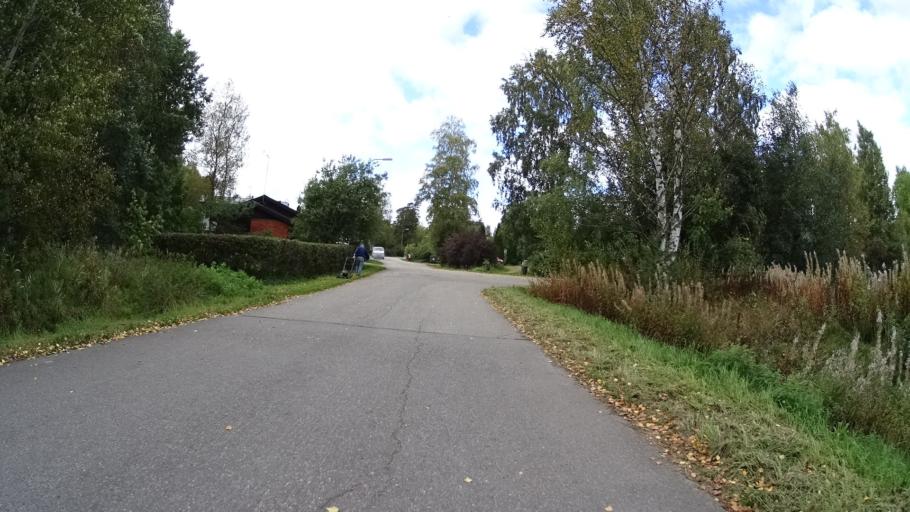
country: FI
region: Uusimaa
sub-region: Helsinki
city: Helsinki
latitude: 60.2492
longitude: 24.9044
